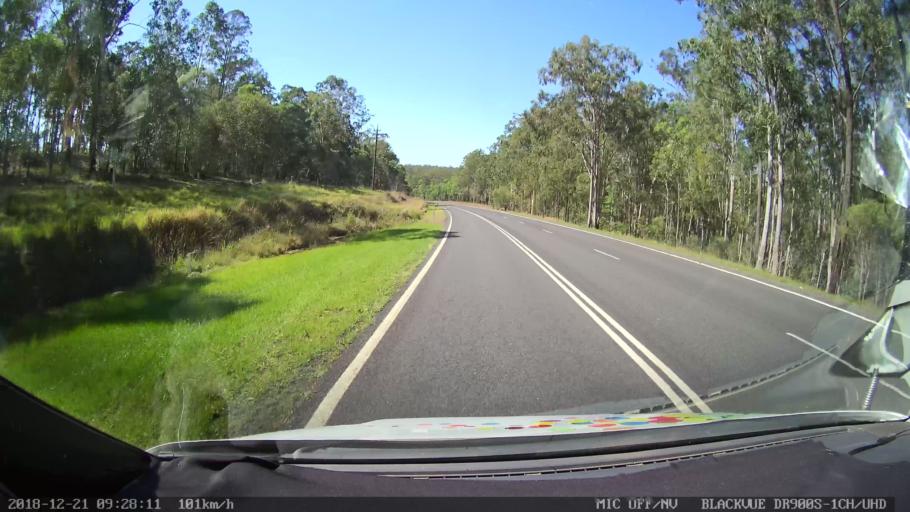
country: AU
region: New South Wales
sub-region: Clarence Valley
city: Maclean
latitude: -29.4136
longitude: 152.9864
